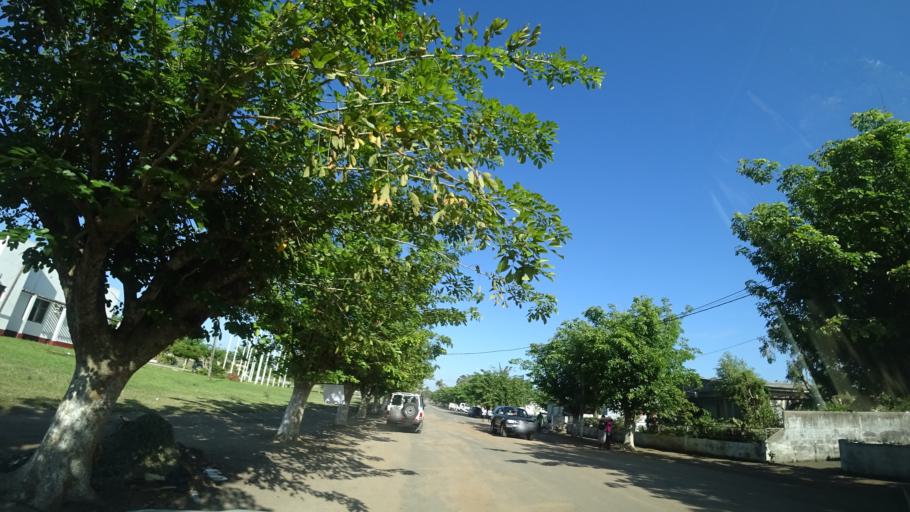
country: MZ
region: Sofala
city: Dondo
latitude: -19.6162
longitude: 34.7432
